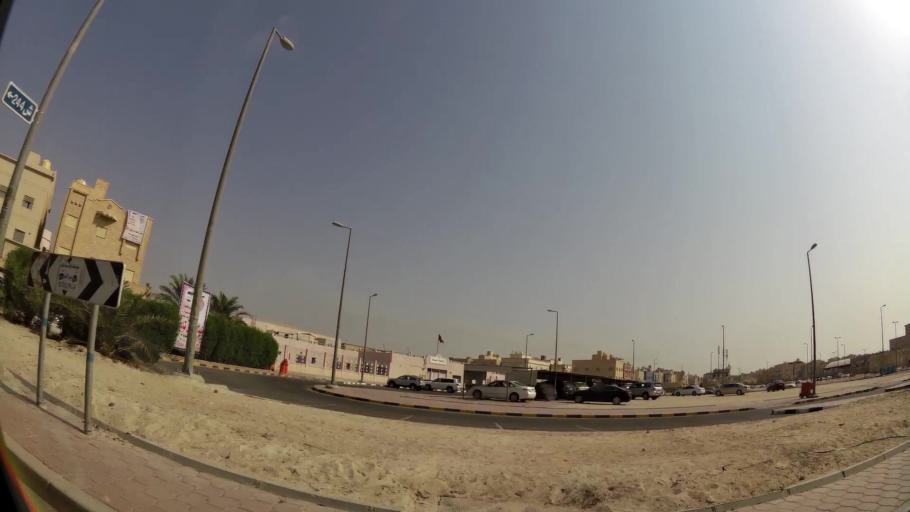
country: KW
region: Muhafazat al Jahra'
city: Al Jahra'
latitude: 29.3391
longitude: 47.7678
